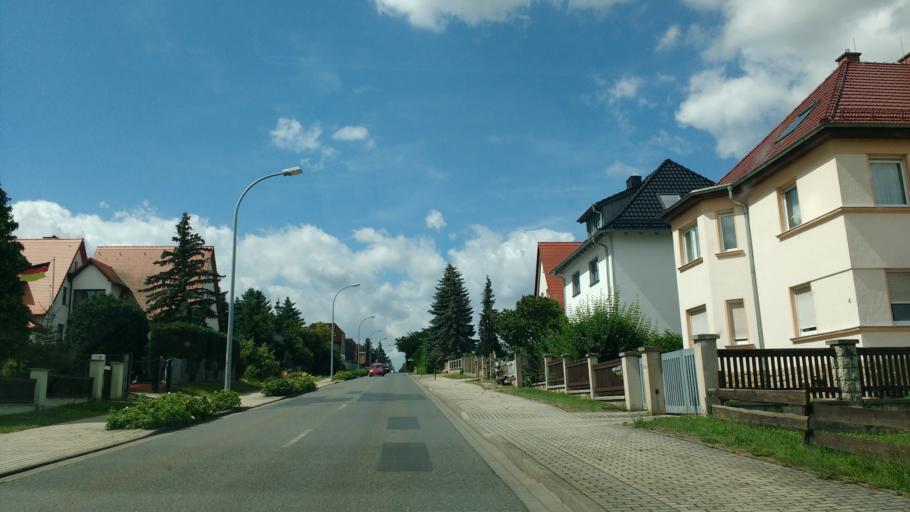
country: DE
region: Saxony-Anhalt
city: Zeitz
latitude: 51.0383
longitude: 12.1375
